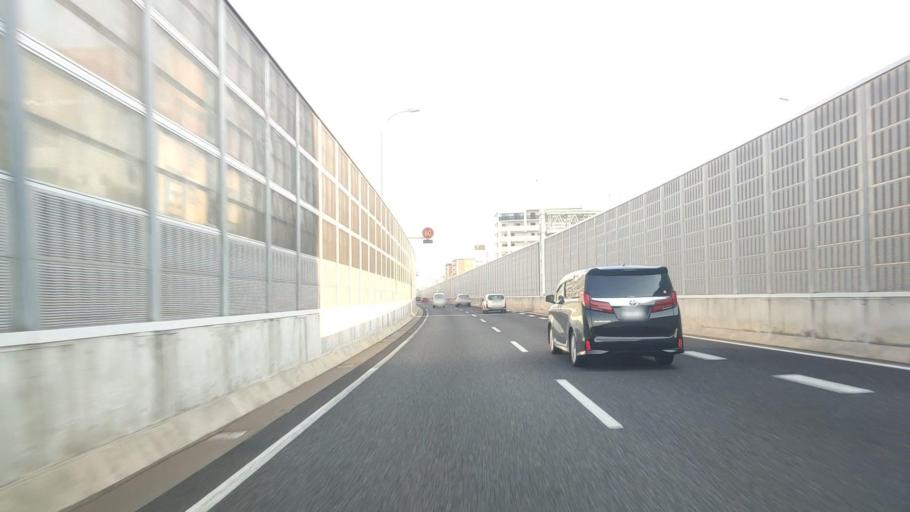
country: JP
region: Aichi
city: Nagoya-shi
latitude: 35.1971
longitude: 136.8906
